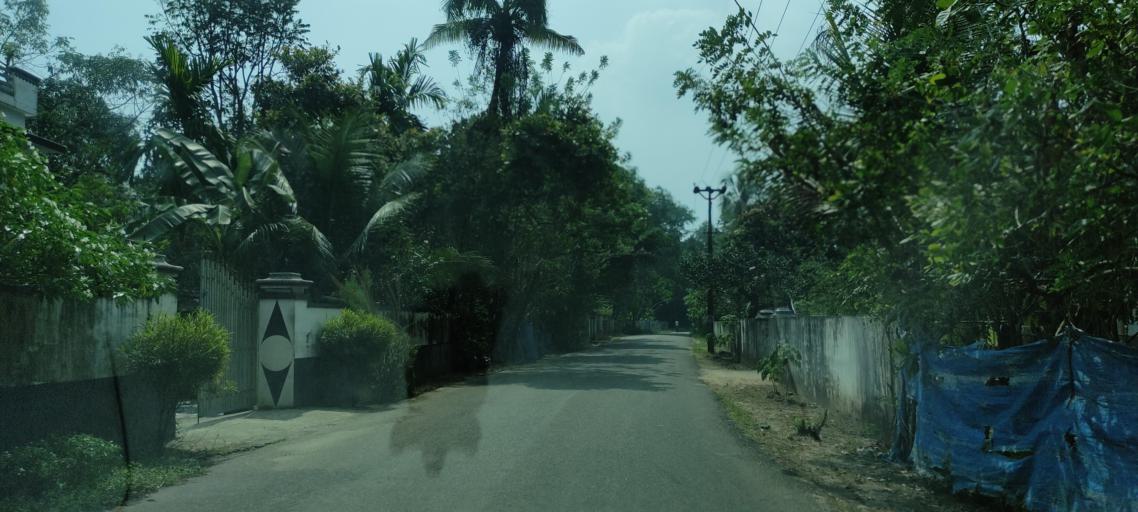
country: IN
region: Kerala
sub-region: Alappuzha
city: Shertallai
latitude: 9.6277
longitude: 76.3511
